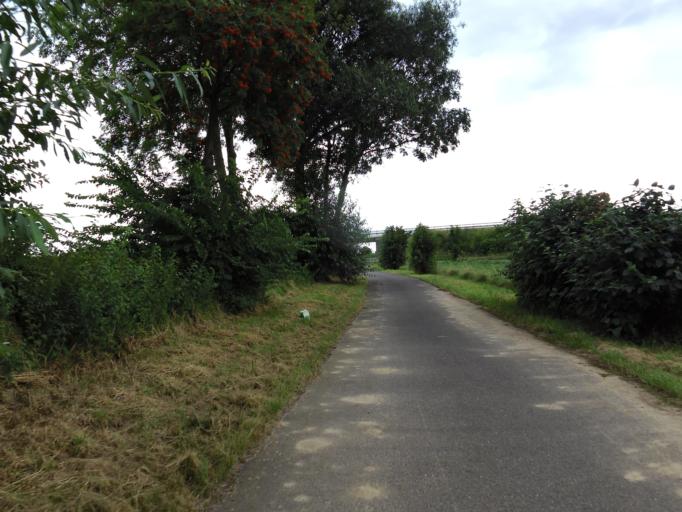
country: DE
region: North Rhine-Westphalia
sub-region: Regierungsbezirk Koln
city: Selfkant
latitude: 51.0147
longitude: 5.9652
